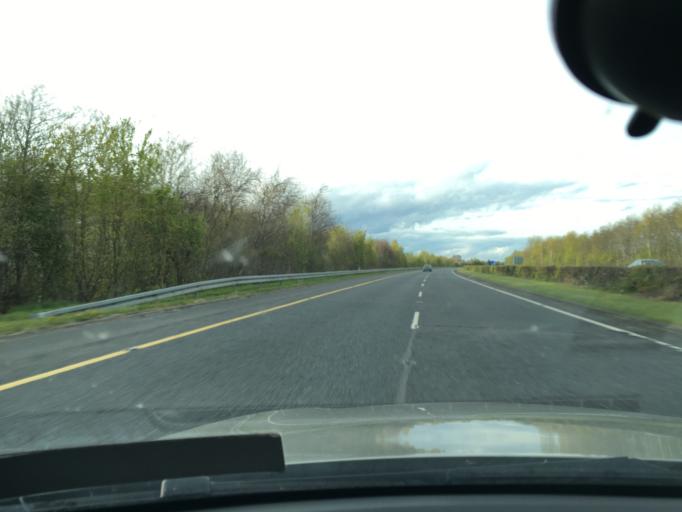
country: IE
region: Leinster
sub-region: Lu
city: Castlebellingham
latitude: 53.8804
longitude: -6.4300
